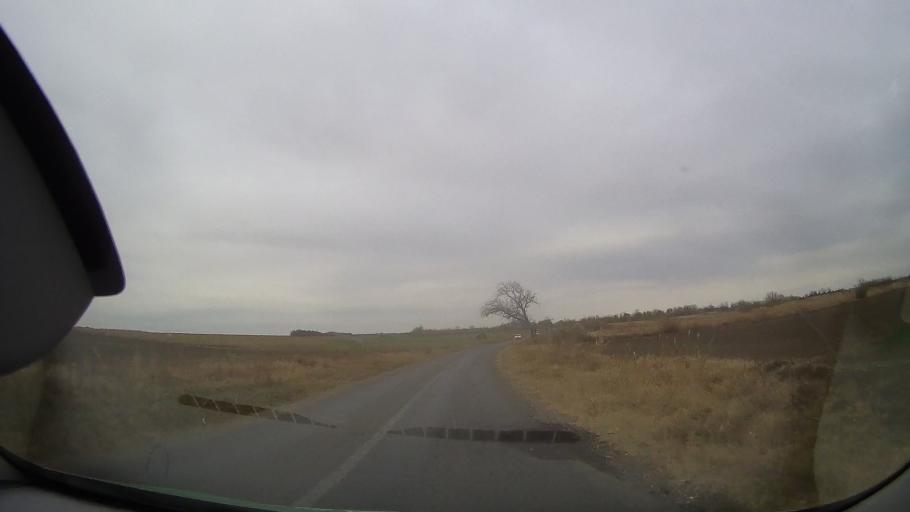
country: RO
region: Buzau
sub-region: Comuna Rusetu
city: Rusetu
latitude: 44.9688
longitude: 27.1864
